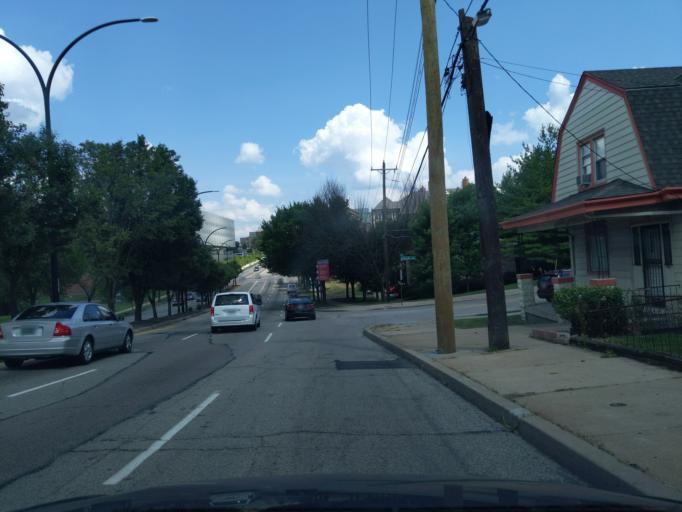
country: US
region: Ohio
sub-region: Hamilton County
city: Saint Bernard
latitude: 39.1353
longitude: -84.5078
